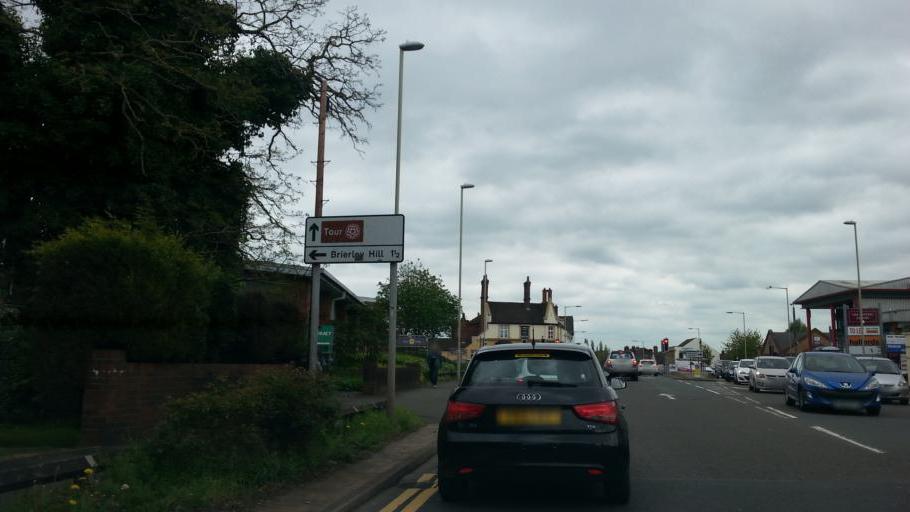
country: GB
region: England
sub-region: Dudley
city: Stourbridge
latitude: 52.4714
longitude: -2.1550
